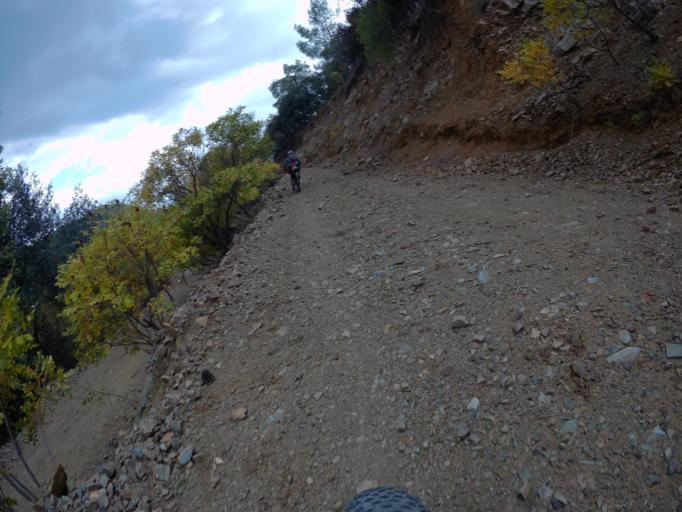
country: CY
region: Lefkosia
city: Kakopetria
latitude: 34.9120
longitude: 32.8001
